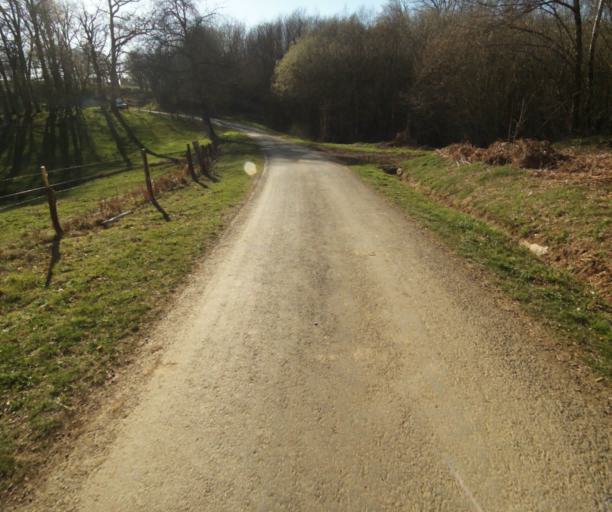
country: FR
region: Limousin
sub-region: Departement de la Correze
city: Seilhac
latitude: 45.3861
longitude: 1.6926
